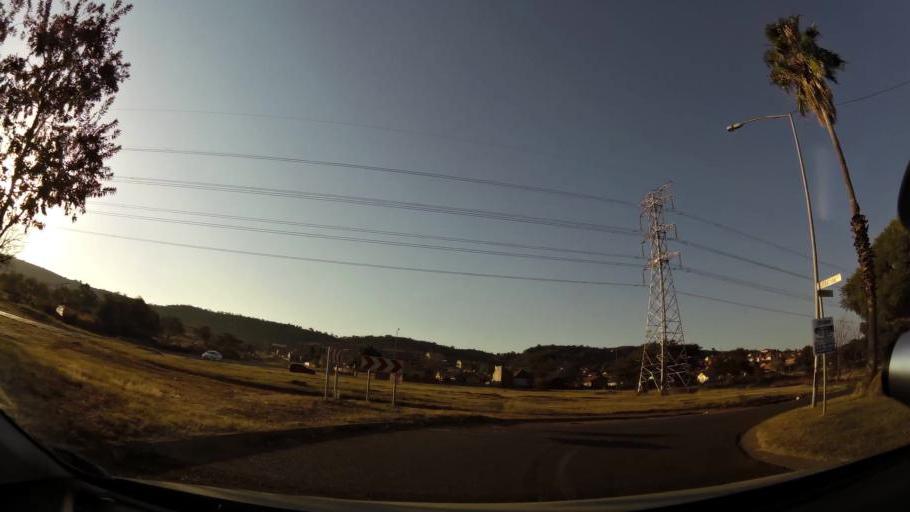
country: ZA
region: Gauteng
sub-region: City of Tshwane Metropolitan Municipality
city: Pretoria
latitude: -25.7364
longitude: 28.1174
